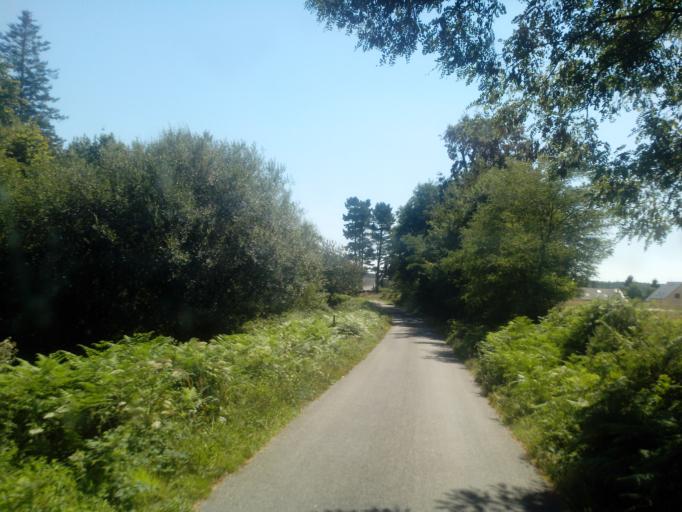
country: FR
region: Brittany
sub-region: Departement du Morbihan
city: Molac
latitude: 47.7237
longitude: -2.4030
